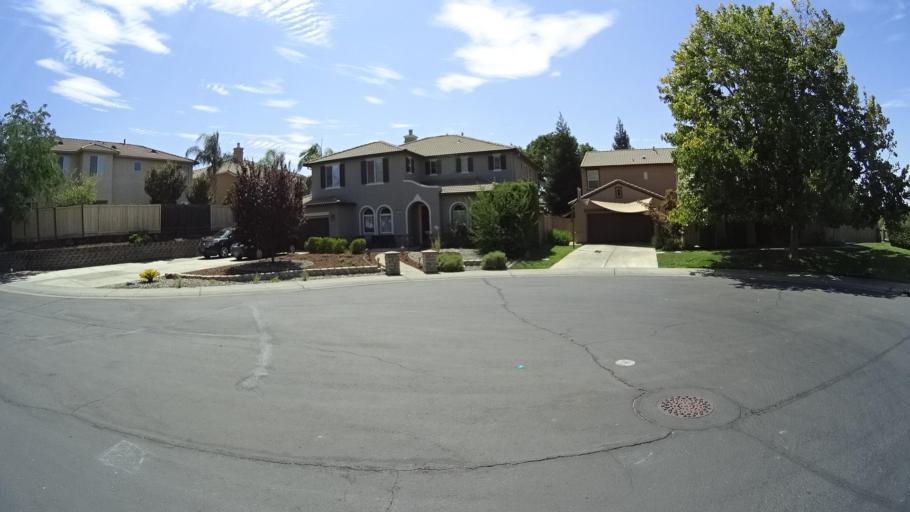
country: US
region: California
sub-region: Placer County
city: Rocklin
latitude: 38.8054
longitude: -121.2847
